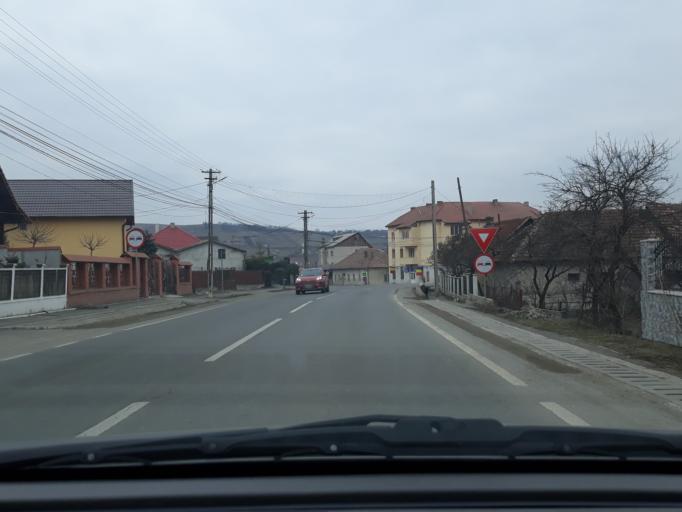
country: RO
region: Salaj
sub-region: Comuna Hereclean
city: Hereclean
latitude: 47.2404
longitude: 22.9911
